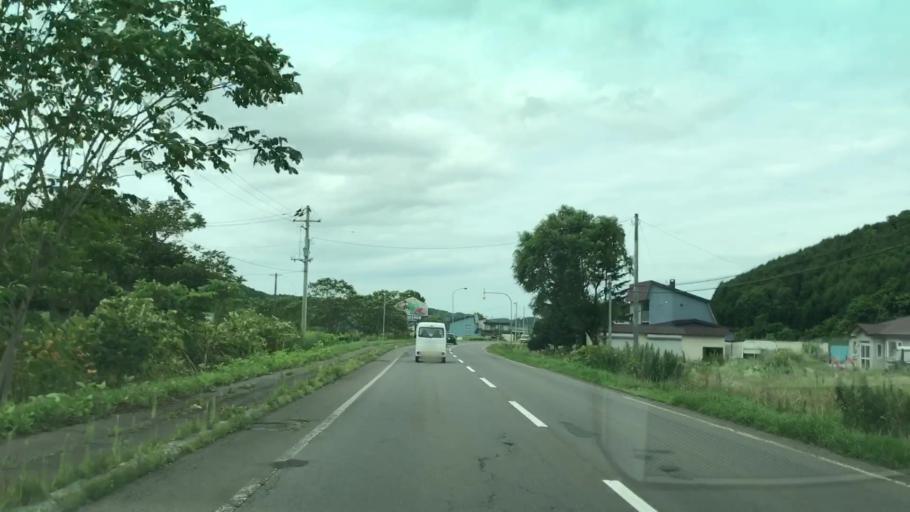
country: JP
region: Hokkaido
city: Iwanai
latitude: 42.9668
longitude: 140.6869
